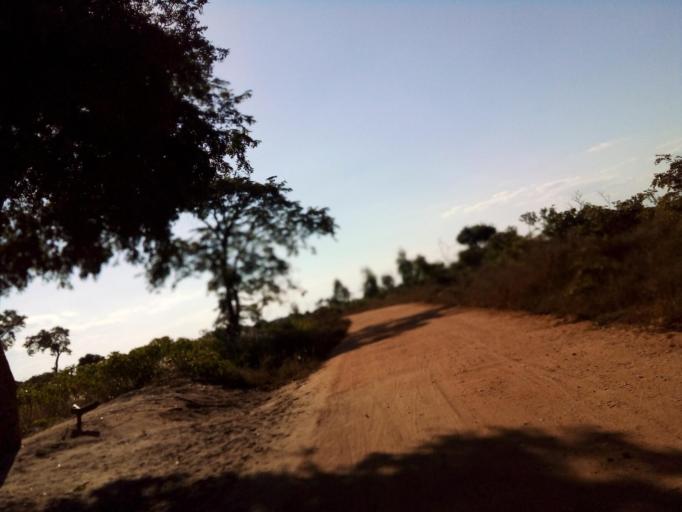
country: MZ
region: Zambezia
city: Quelimane
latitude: -17.5004
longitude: 36.5794
